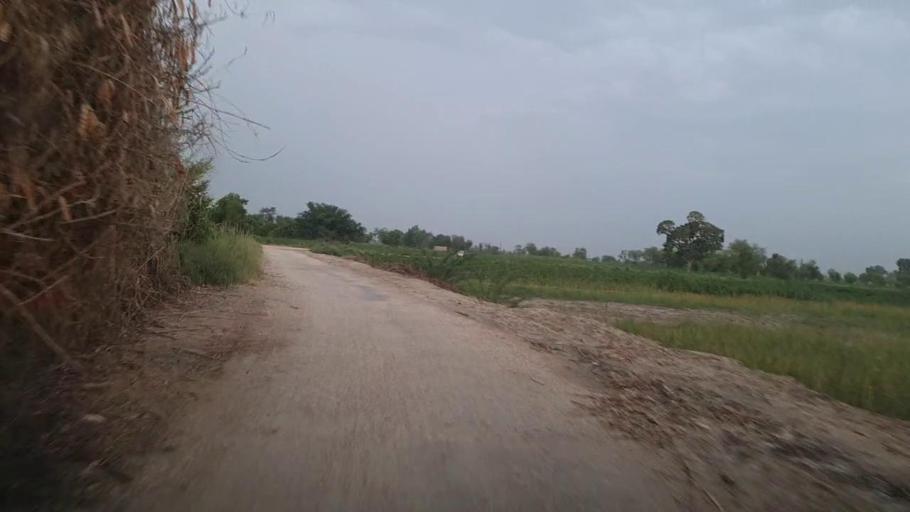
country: PK
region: Sindh
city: Karaundi
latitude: 27.0082
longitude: 68.3432
